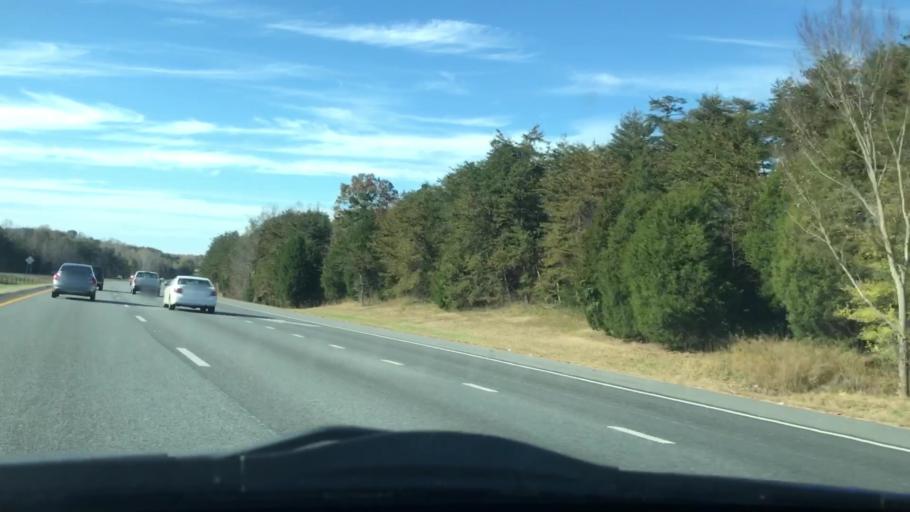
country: US
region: North Carolina
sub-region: Guilford County
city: High Point
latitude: 36.0186
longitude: -80.0460
